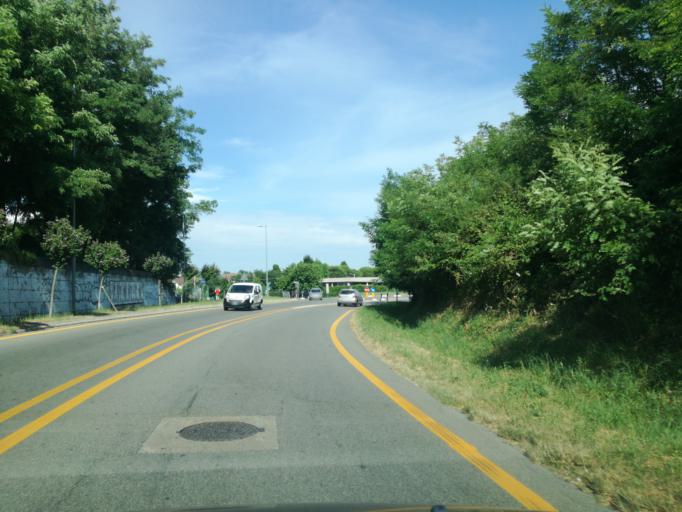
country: IT
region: Lombardy
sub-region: Provincia di Monza e Brianza
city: Bernareggio
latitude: 45.6498
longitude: 9.3958
